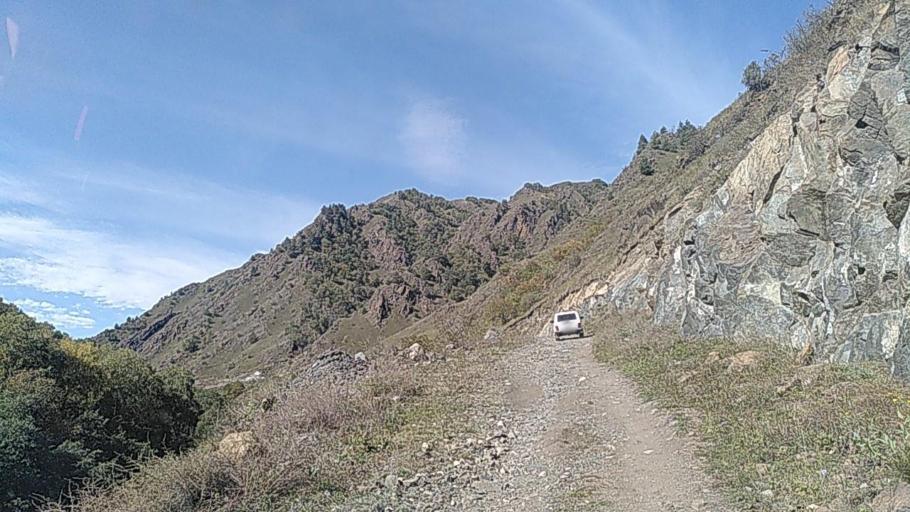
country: RU
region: Kabardino-Balkariya
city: Kamennomostskoye
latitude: 43.7227
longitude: 42.8514
